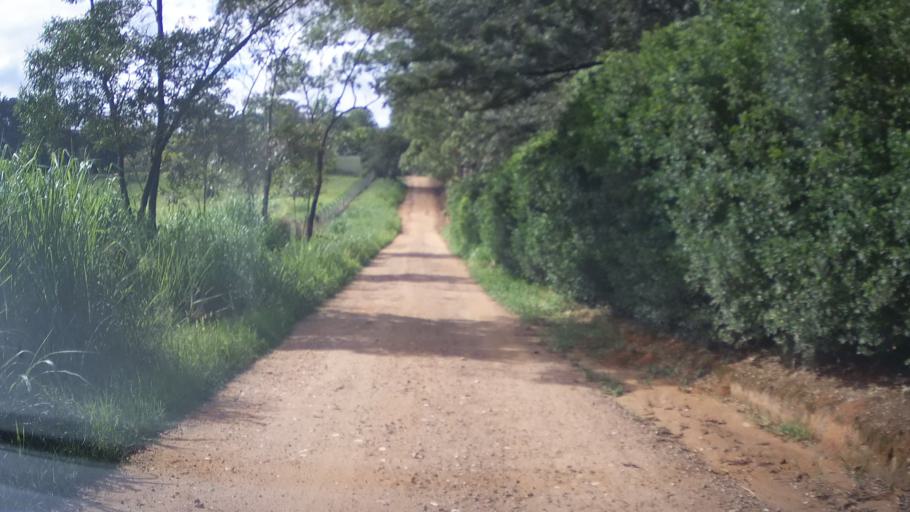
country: BR
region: Sao Paulo
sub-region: Itupeva
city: Itupeva
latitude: -23.2051
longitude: -47.0210
